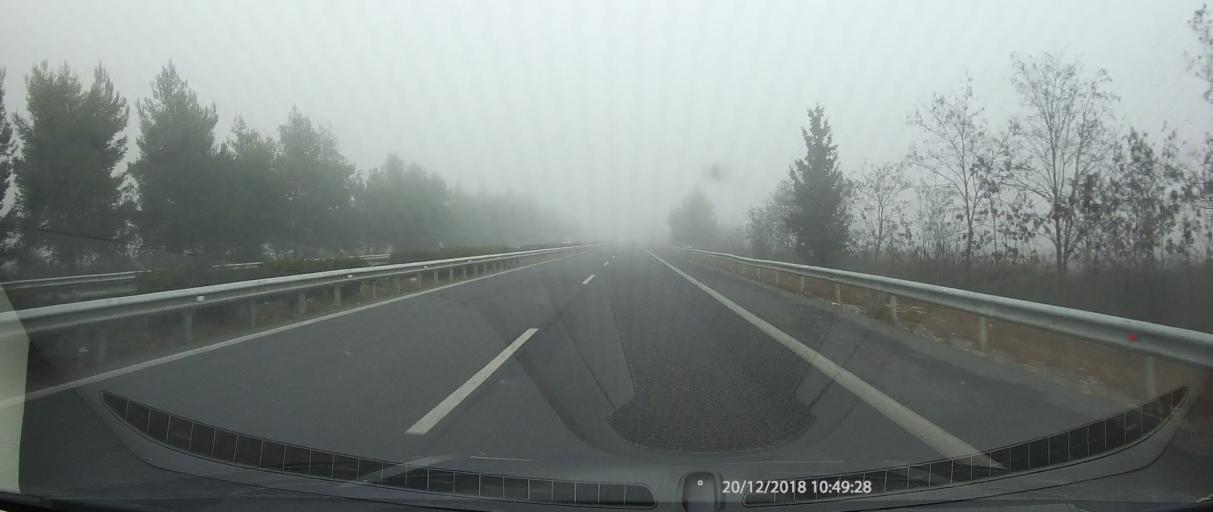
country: GR
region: Peloponnese
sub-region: Nomos Arkadias
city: Tripoli
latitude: 37.5408
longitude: 22.4156
